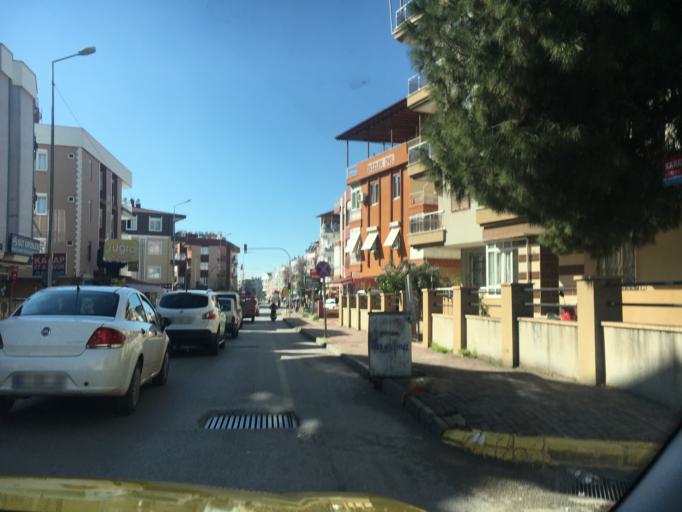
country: TR
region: Antalya
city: Antalya
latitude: 36.9158
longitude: 30.7066
